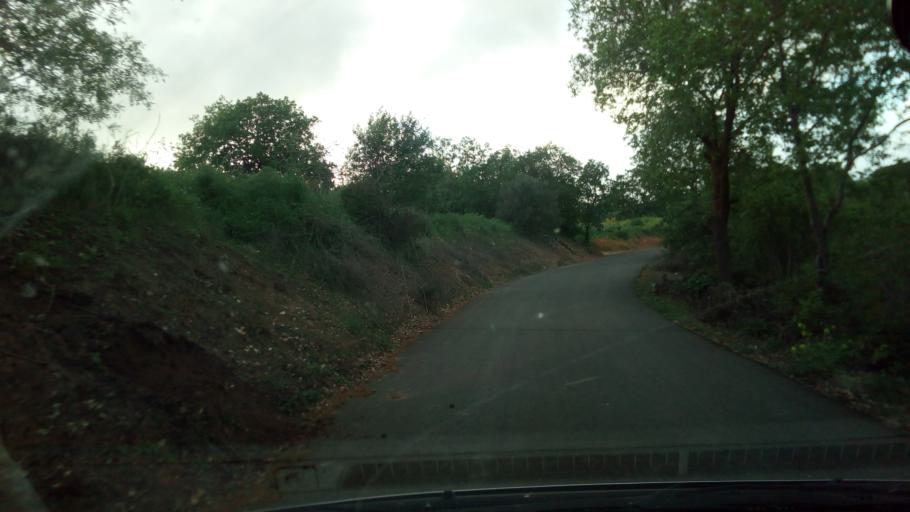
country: CY
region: Pafos
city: Polis
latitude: 34.9982
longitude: 32.5100
